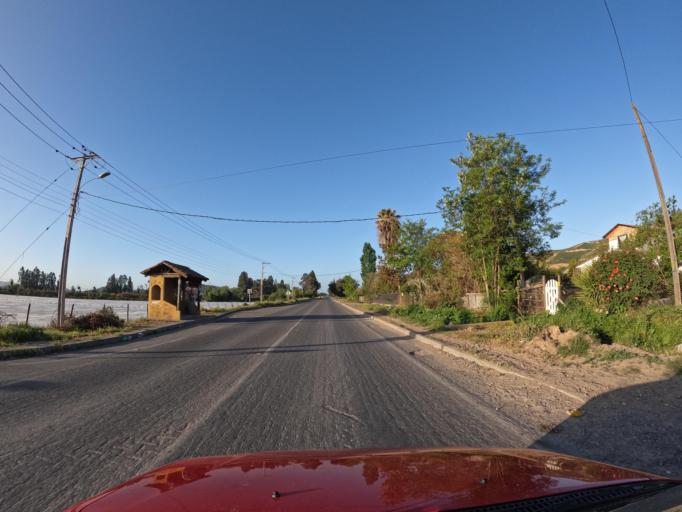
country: CL
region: O'Higgins
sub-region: Provincia de Colchagua
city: Santa Cruz
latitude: -34.3471
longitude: -71.4067
